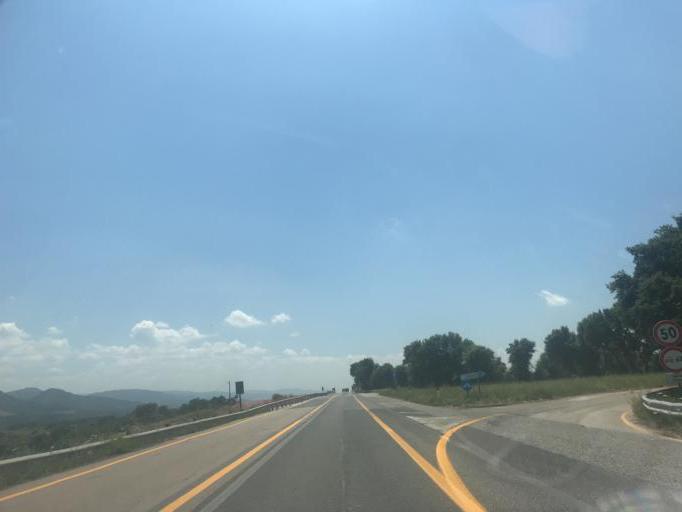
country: IT
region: Sardinia
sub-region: Provincia di Olbia-Tempio
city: Monti
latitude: 40.8020
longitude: 9.2792
